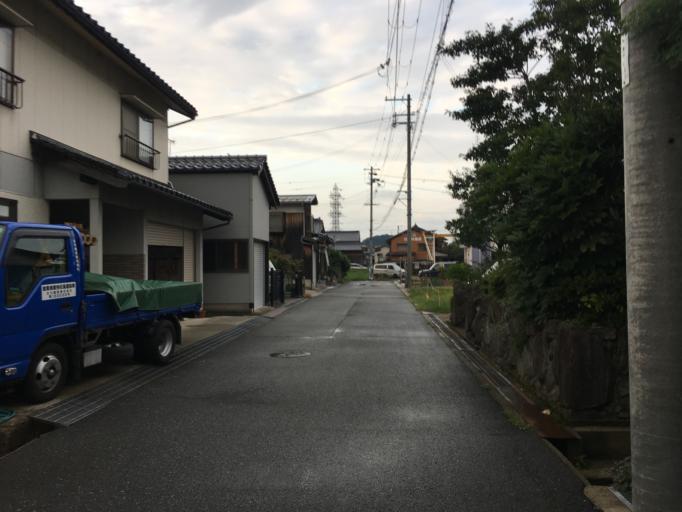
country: JP
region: Hyogo
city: Toyooka
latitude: 35.6340
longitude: 134.6284
